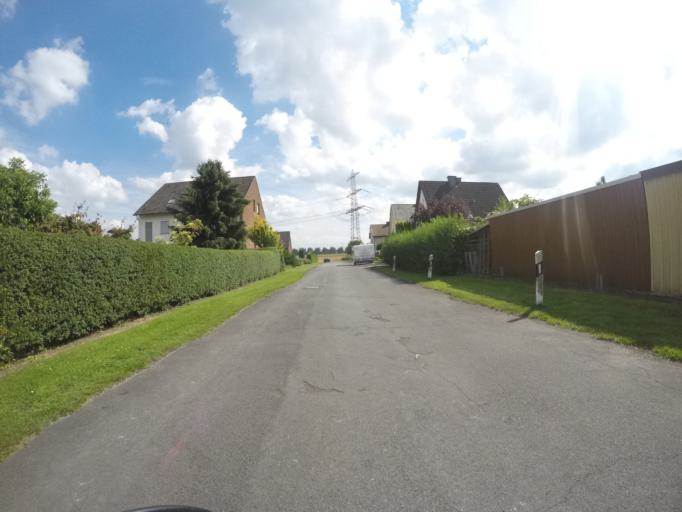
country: DE
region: North Rhine-Westphalia
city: Enger
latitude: 52.1160
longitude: 8.5790
